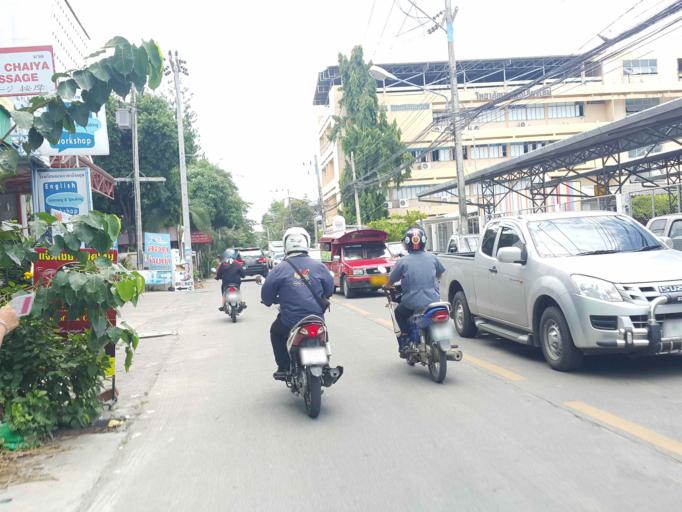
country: TH
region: Chiang Mai
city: Chiang Mai
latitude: 18.7932
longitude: 98.9823
